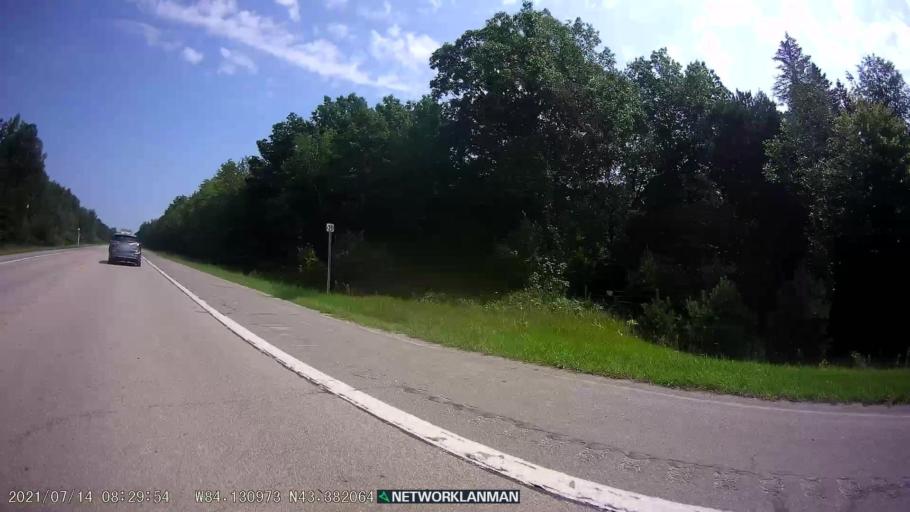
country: US
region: Michigan
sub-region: Saginaw County
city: Shields
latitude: 43.3825
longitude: -84.1310
